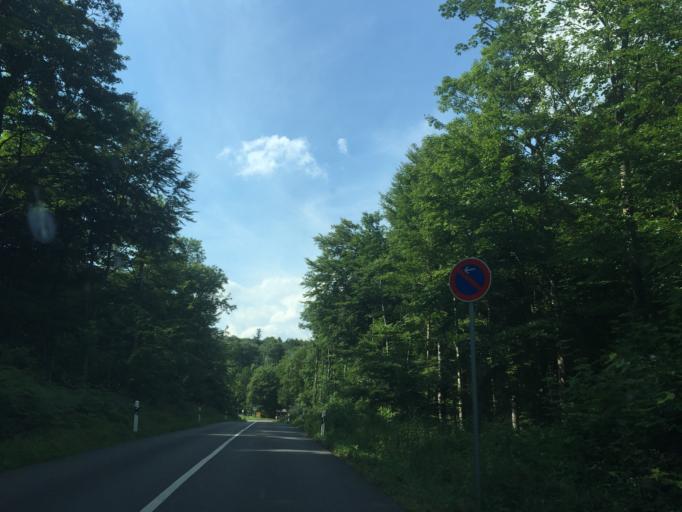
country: DE
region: Baden-Wuerttemberg
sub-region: Karlsruhe Region
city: Gaiberg
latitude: 49.3786
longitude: 8.7250
